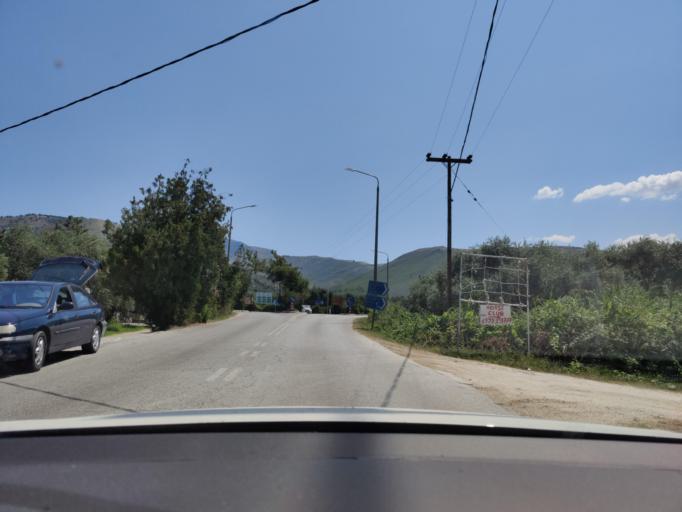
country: GR
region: East Macedonia and Thrace
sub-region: Nomos Kavalas
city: Prinos
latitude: 40.7565
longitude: 24.5782
